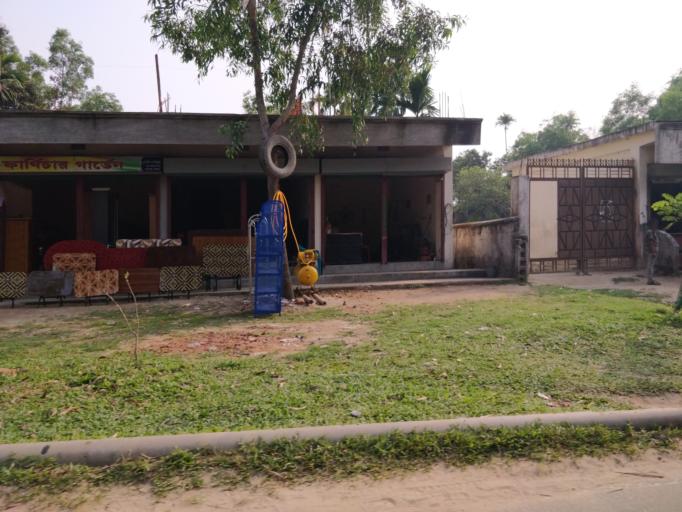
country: IN
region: Tripura
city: Khowai
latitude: 24.1300
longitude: 91.3682
